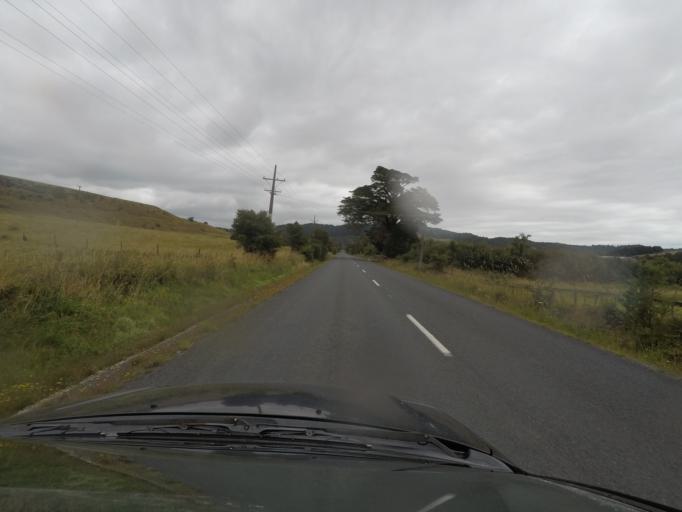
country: NZ
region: Auckland
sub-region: Auckland
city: Warkworth
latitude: -36.2862
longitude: 174.6482
